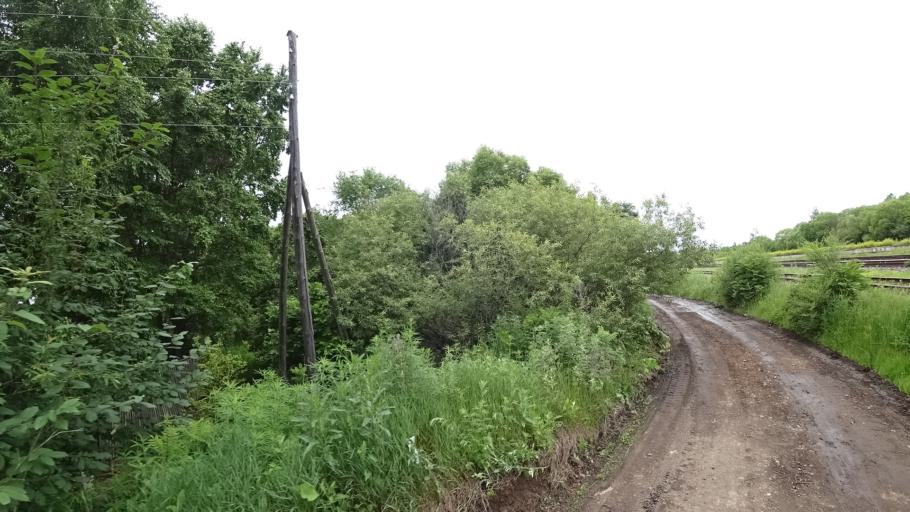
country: RU
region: Primorskiy
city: Novosysoyevka
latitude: 44.2075
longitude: 133.3433
